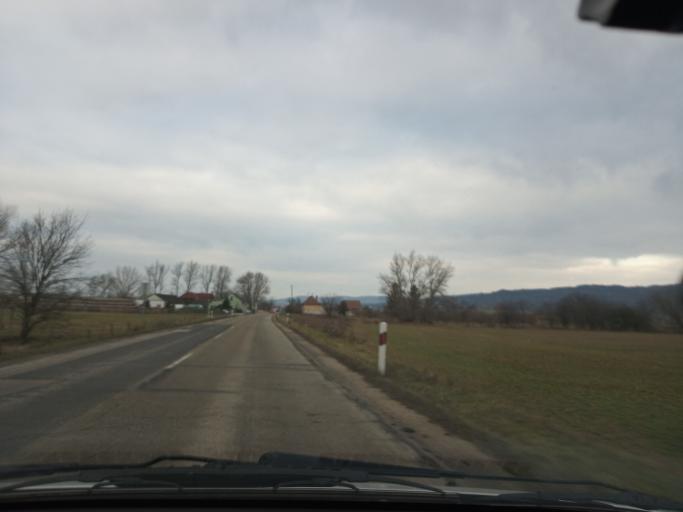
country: HU
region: Komarom-Esztergom
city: Esztergom
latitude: 47.7660
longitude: 18.7371
